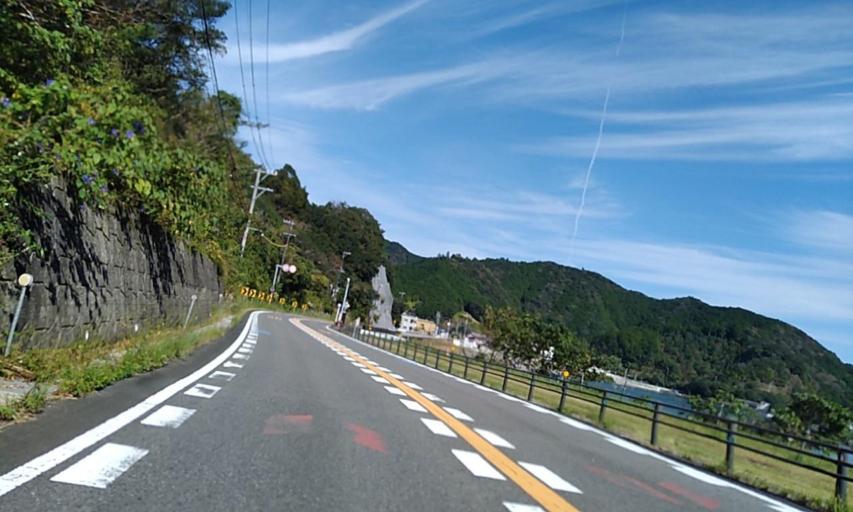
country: JP
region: Mie
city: Owase
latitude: 34.1612
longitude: 136.2774
